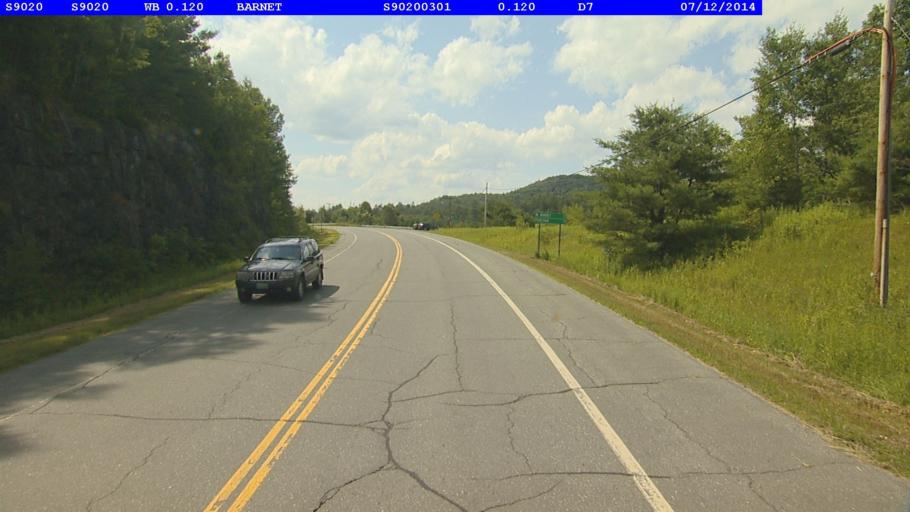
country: US
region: Vermont
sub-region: Caledonia County
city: Saint Johnsbury
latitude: 44.2998
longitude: -72.0585
